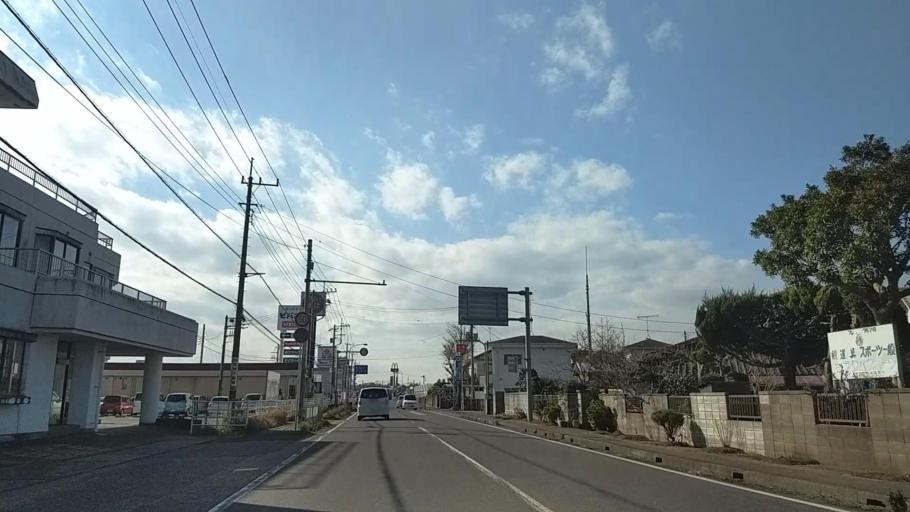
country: JP
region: Chiba
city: Yokaichiba
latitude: 35.6617
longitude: 140.4868
